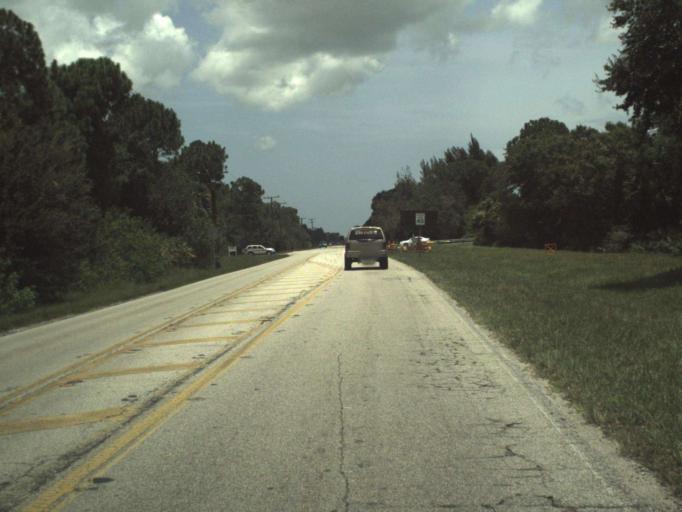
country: US
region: Florida
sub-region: Saint Lucie County
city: Fort Pierce South
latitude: 27.3745
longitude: -80.3804
